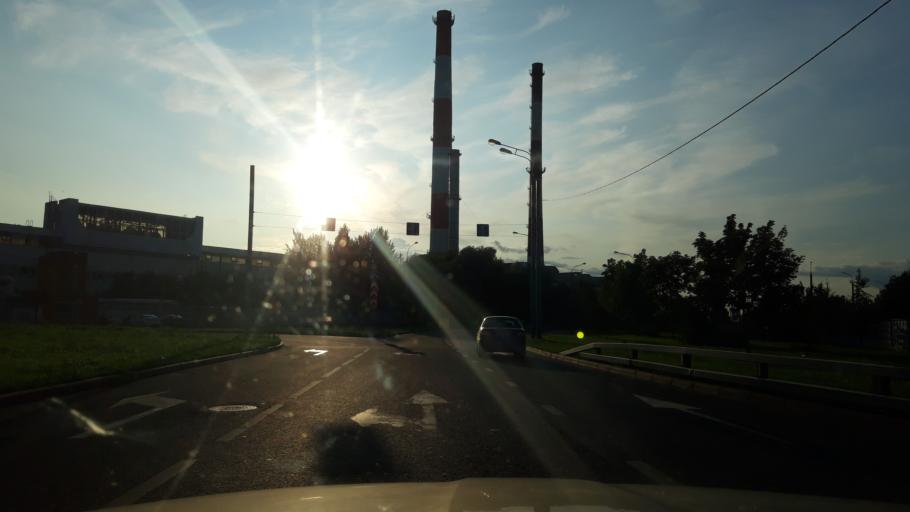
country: RU
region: Moscow
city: Zelenograd
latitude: 55.9908
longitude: 37.1675
